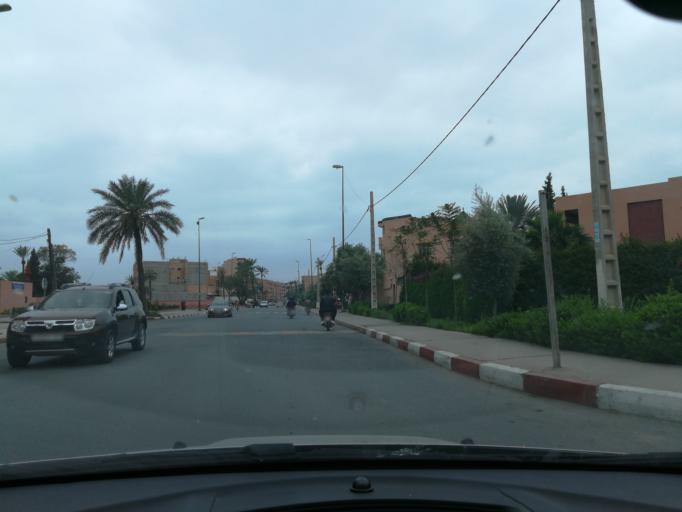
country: MA
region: Marrakech-Tensift-Al Haouz
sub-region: Marrakech
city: Marrakesh
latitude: 31.6491
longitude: -8.0044
